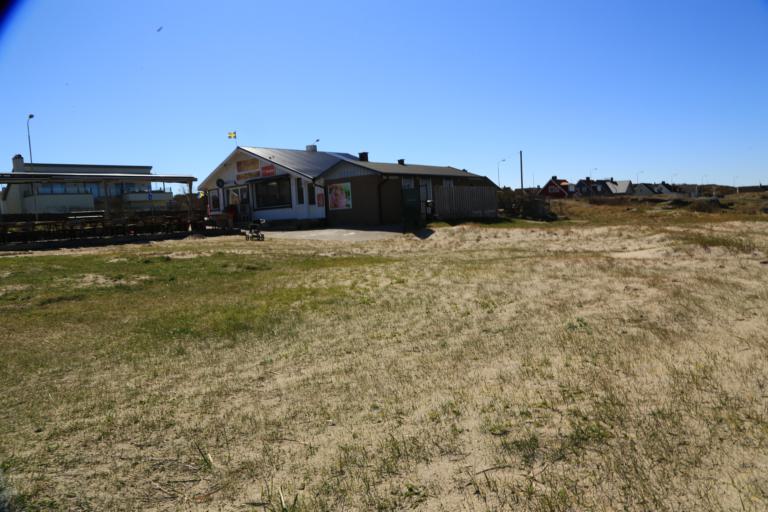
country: SE
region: Halland
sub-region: Varbergs Kommun
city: Traslovslage
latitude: 57.0627
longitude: 12.2780
